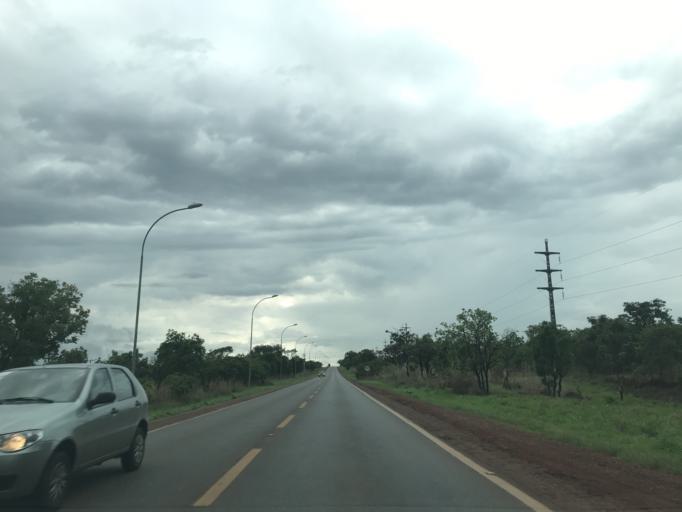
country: BR
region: Goias
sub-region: Planaltina
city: Planaltina
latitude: -15.6182
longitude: -47.7046
